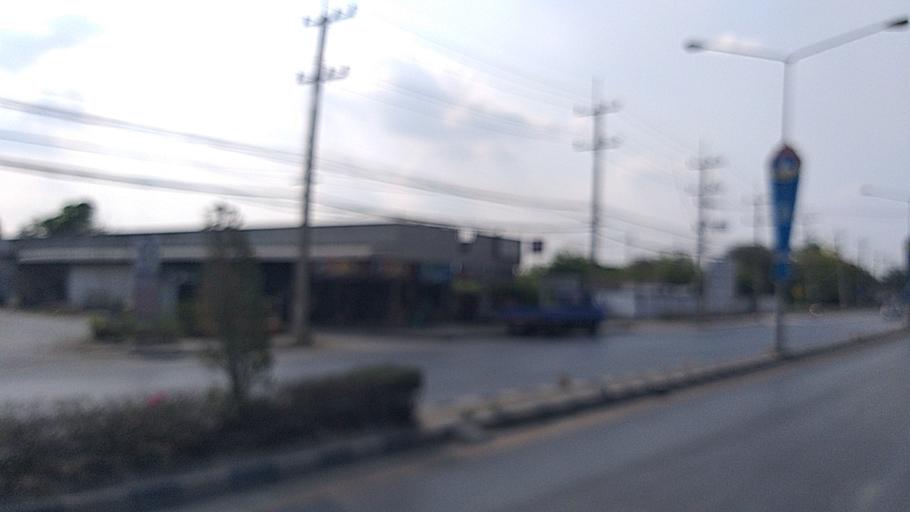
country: TH
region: Pathum Thani
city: Sam Khok
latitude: 14.0697
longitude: 100.5224
